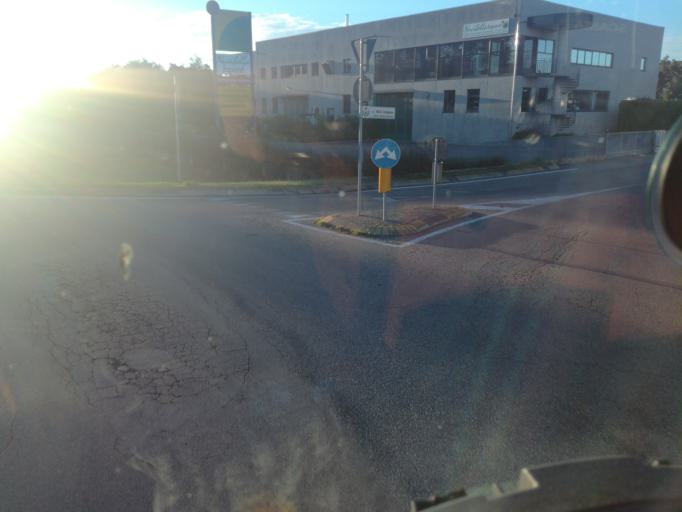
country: IT
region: Lombardy
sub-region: Provincia di Monza e Brianza
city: Bovisio-Masciago
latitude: 45.6186
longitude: 9.1596
